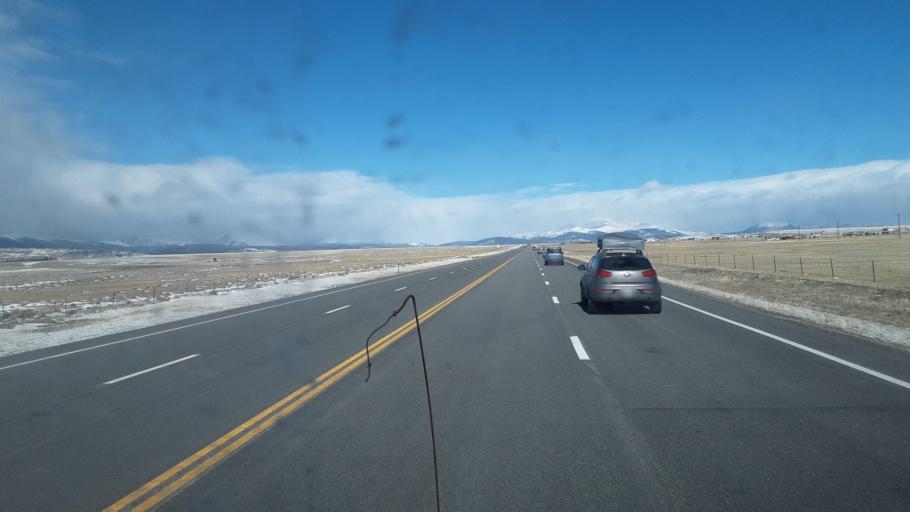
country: US
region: Colorado
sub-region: Park County
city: Fairplay
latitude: 39.1085
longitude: -105.9905
